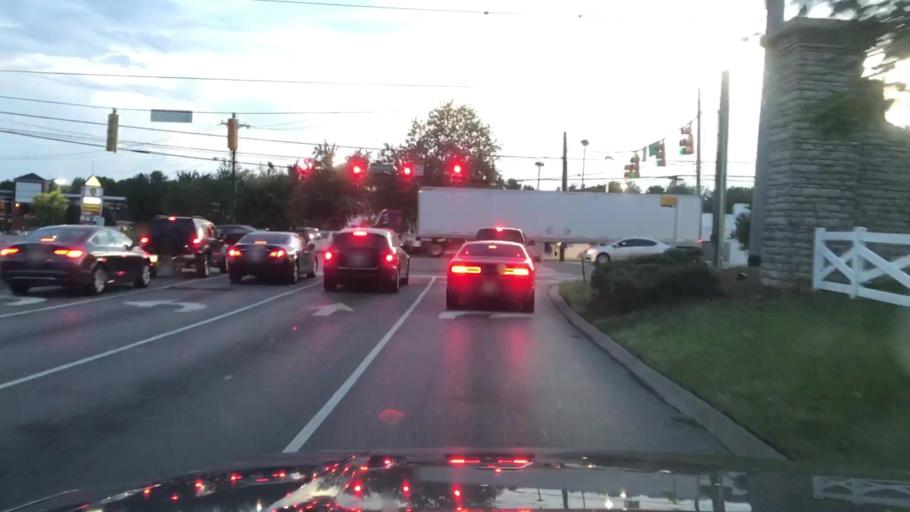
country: US
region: Tennessee
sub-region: Rutherford County
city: La Vergne
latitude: 36.0871
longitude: -86.6482
